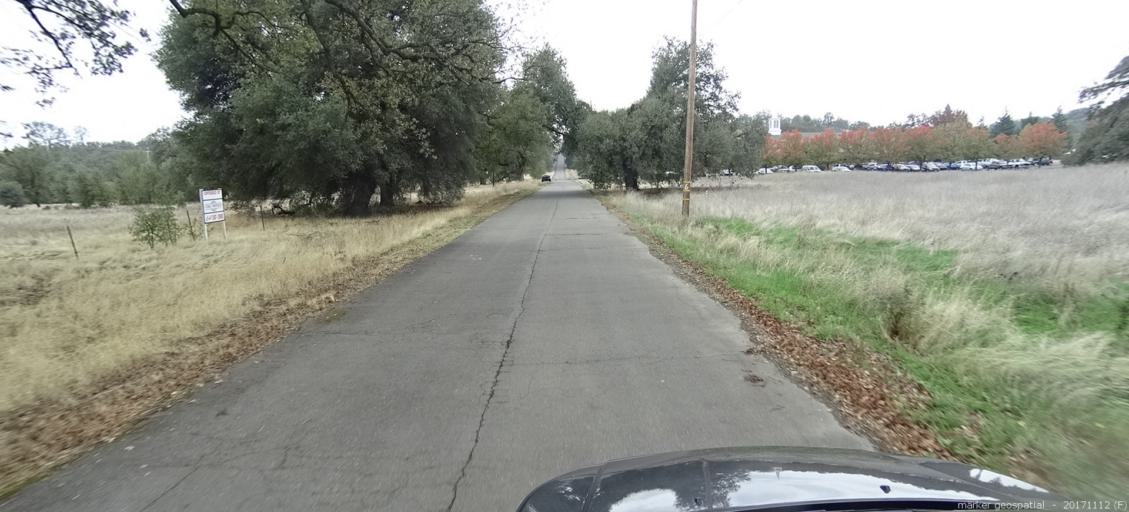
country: US
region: California
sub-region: Shasta County
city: Palo Cedro
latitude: 40.5566
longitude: -122.2407
